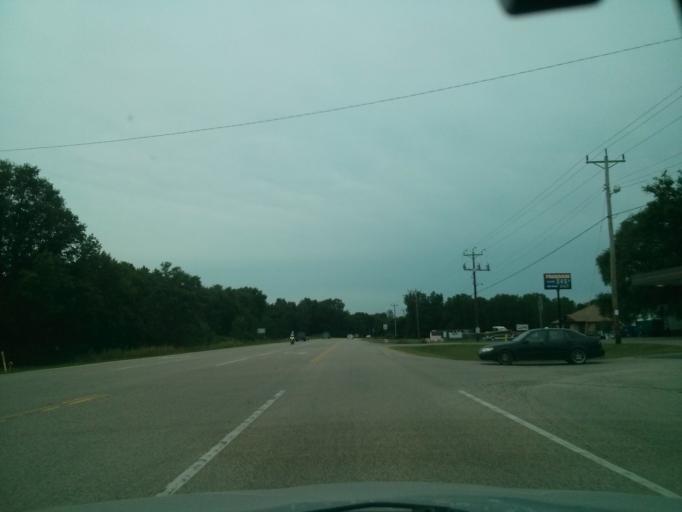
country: US
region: Minnesota
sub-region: Washington County
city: Lake Saint Croix Beach
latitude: 44.9204
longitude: -92.7736
